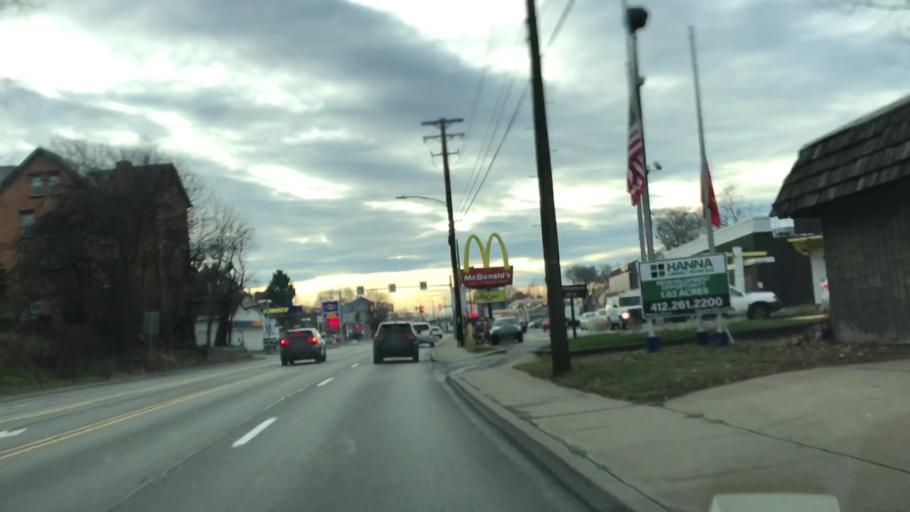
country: US
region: Pennsylvania
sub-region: Allegheny County
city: Avalon
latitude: 40.4928
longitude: -80.0624
